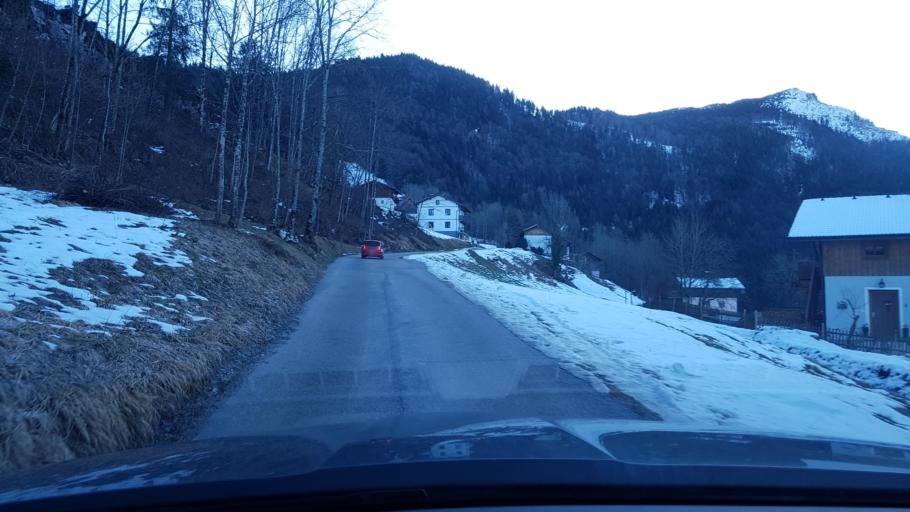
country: AT
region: Salzburg
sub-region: Politischer Bezirk Hallein
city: Scheffau am Tennengebirge
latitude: 47.6458
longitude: 13.2275
